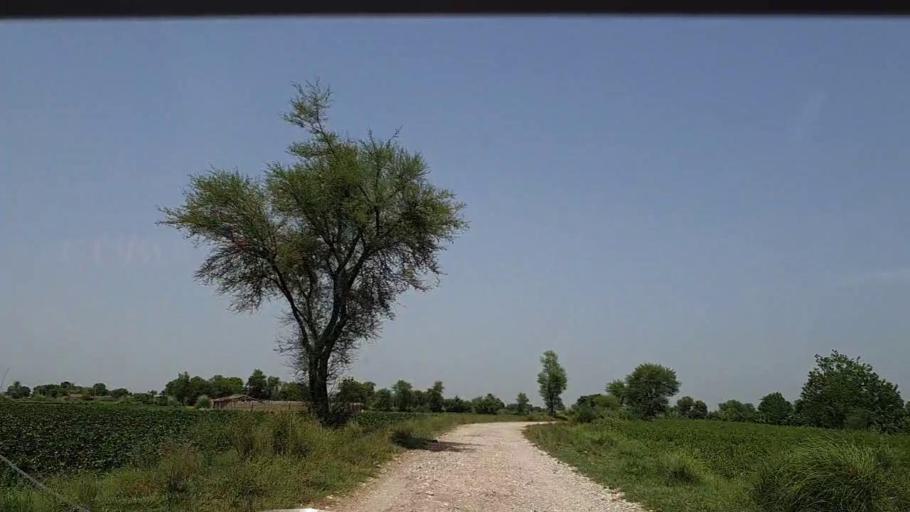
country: PK
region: Sindh
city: Tharu Shah
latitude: 26.9451
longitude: 68.0434
